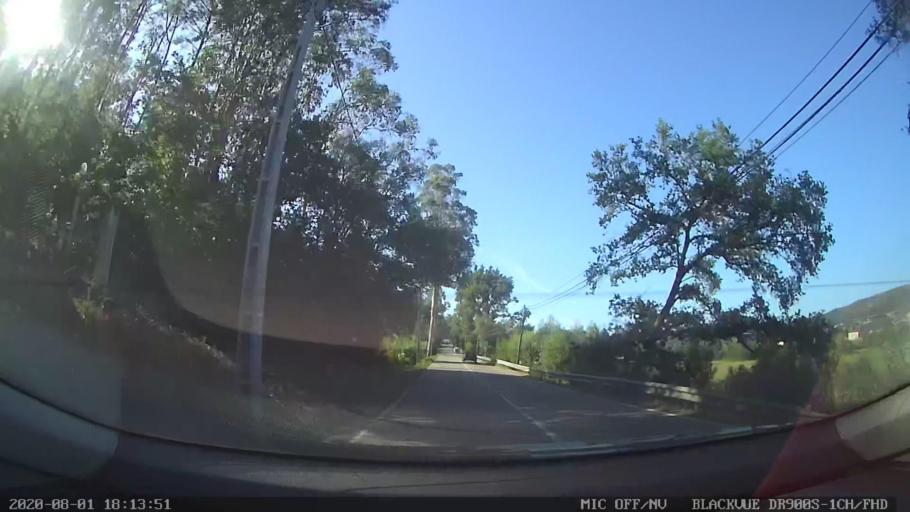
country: PT
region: Porto
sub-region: Pacos de Ferreira
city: Seroa
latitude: 41.2751
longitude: -8.4685
